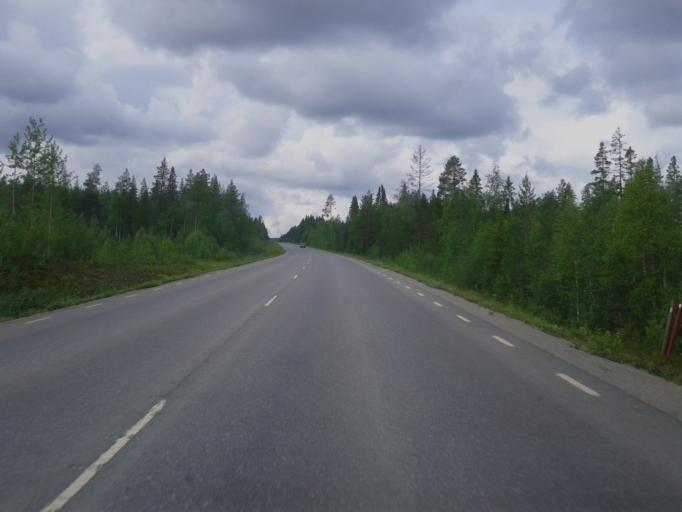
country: SE
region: Vaesterbotten
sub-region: Norsjo Kommun
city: Norsjoe
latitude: 64.9871
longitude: 19.4630
